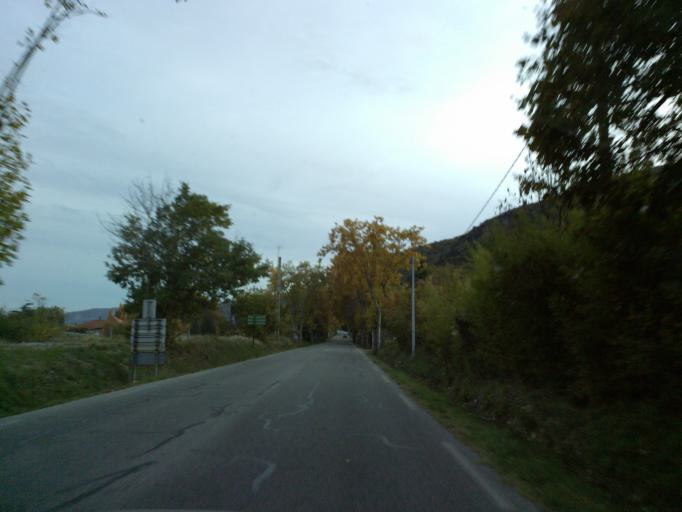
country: FR
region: Provence-Alpes-Cote d'Azur
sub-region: Departement des Alpes-de-Haute-Provence
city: Sisteron
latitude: 44.1780
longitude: 5.9490
